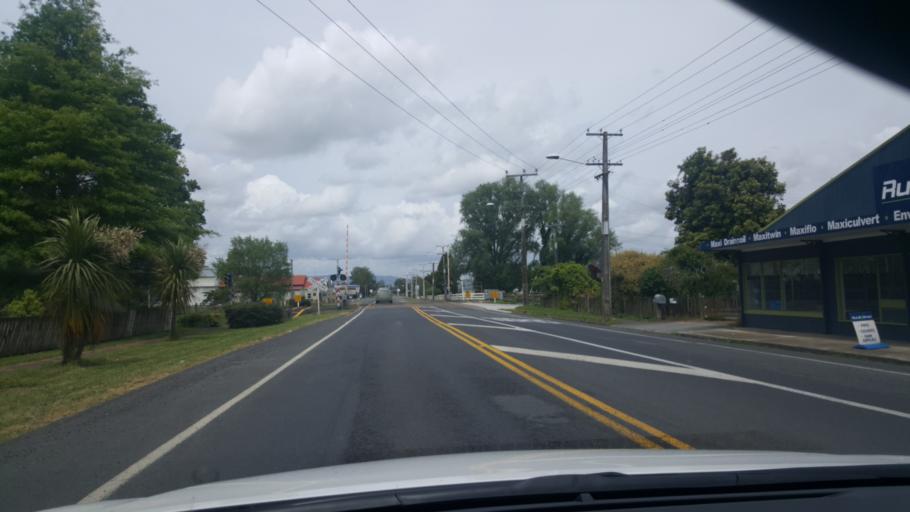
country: NZ
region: Waikato
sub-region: Matamata-Piako District
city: Matamata
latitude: -37.8818
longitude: 175.7593
